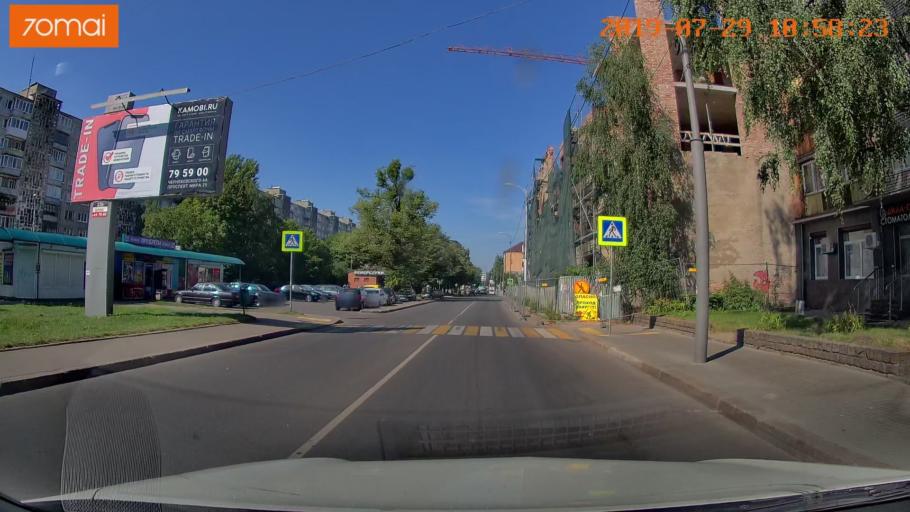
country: RU
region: Kaliningrad
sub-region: Gorod Kaliningrad
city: Kaliningrad
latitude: 54.7128
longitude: 20.5274
